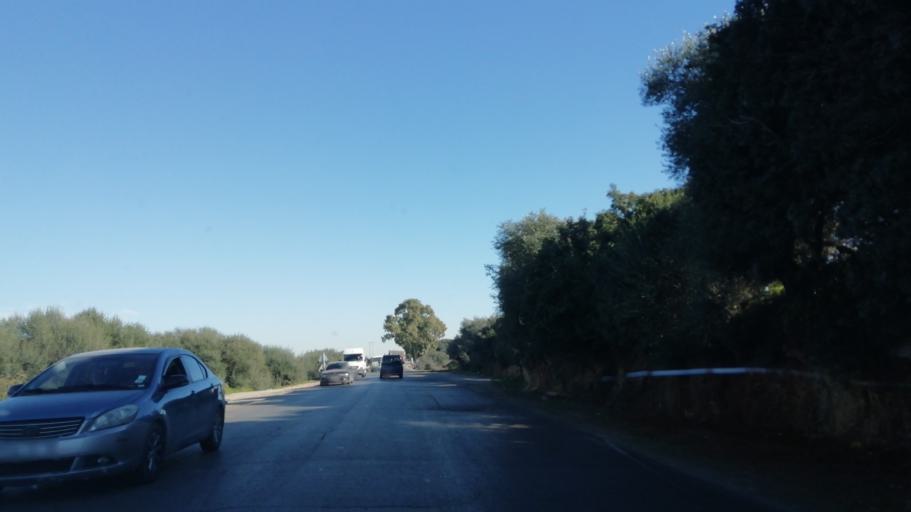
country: DZ
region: Relizane
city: Smala
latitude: 35.6970
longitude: 0.7778
